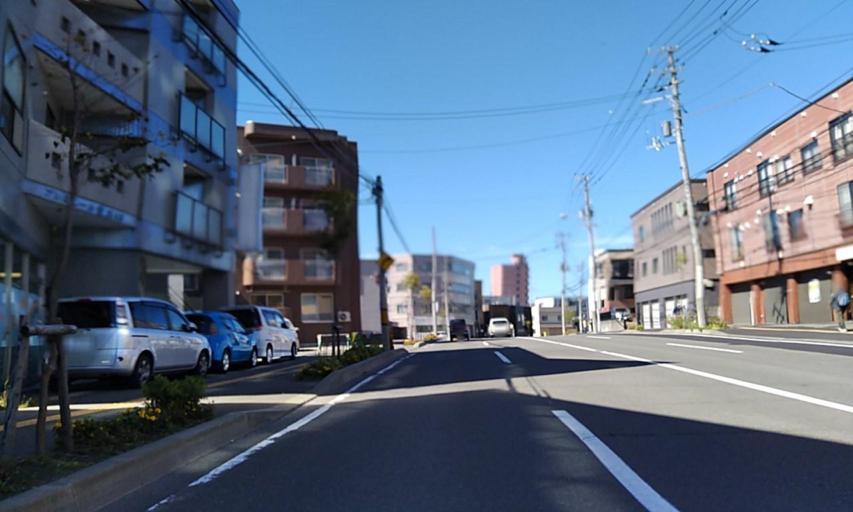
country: JP
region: Hokkaido
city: Sapporo
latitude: 43.0138
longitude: 141.3702
